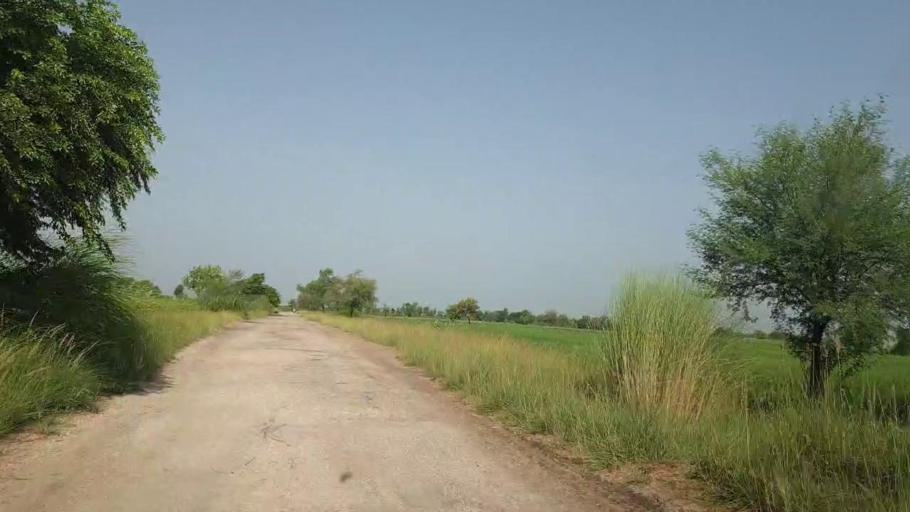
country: PK
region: Sindh
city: Sakrand
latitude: 26.2917
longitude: 68.2253
